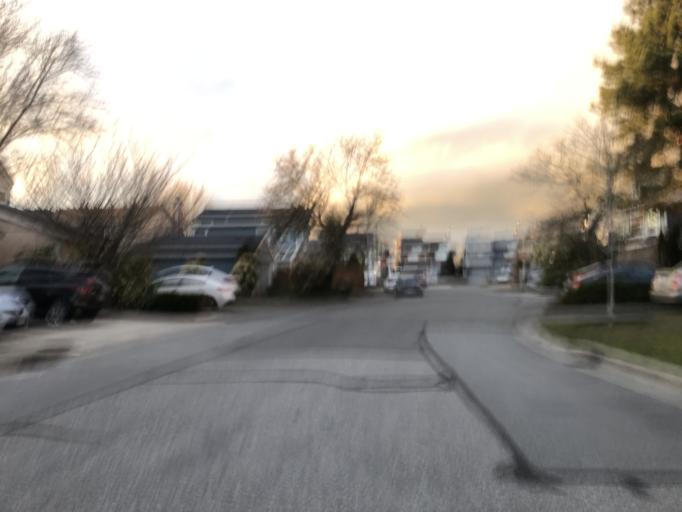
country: CA
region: British Columbia
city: Richmond
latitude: 49.1540
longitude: -123.1176
